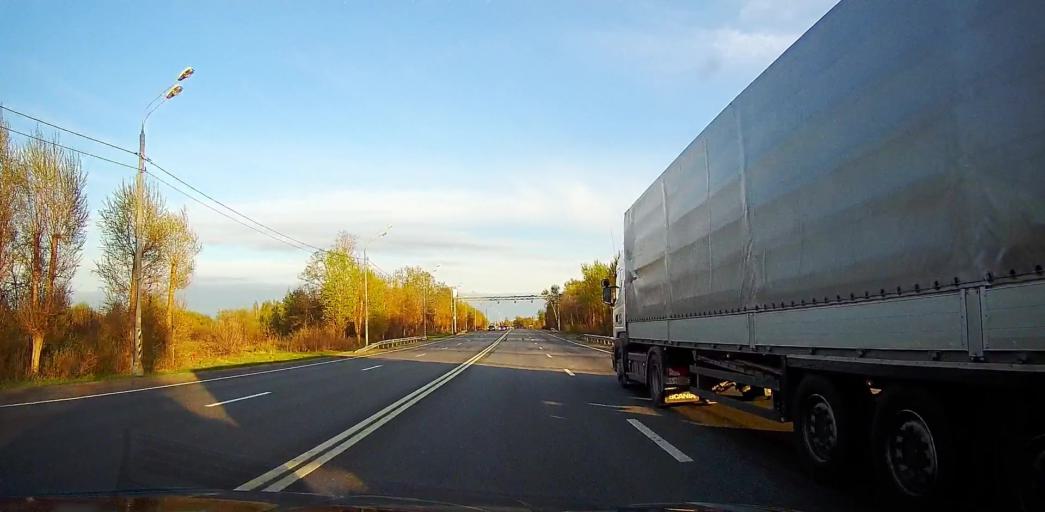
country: RU
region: Moskovskaya
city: Troitskoye
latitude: 55.2589
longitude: 38.5132
